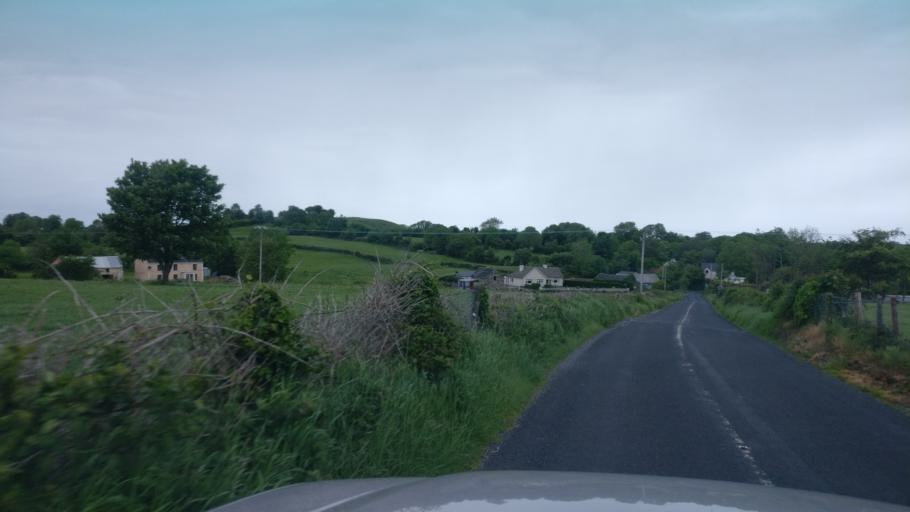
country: IE
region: Connaught
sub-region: County Galway
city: Loughrea
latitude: 53.1202
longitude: -8.4328
